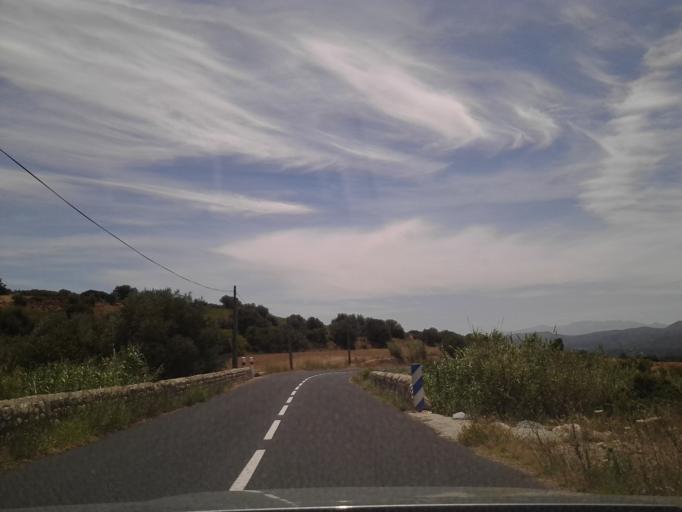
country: FR
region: Languedoc-Roussillon
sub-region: Departement des Pyrenees-Orientales
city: Millas
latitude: 42.7128
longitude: 2.6830
